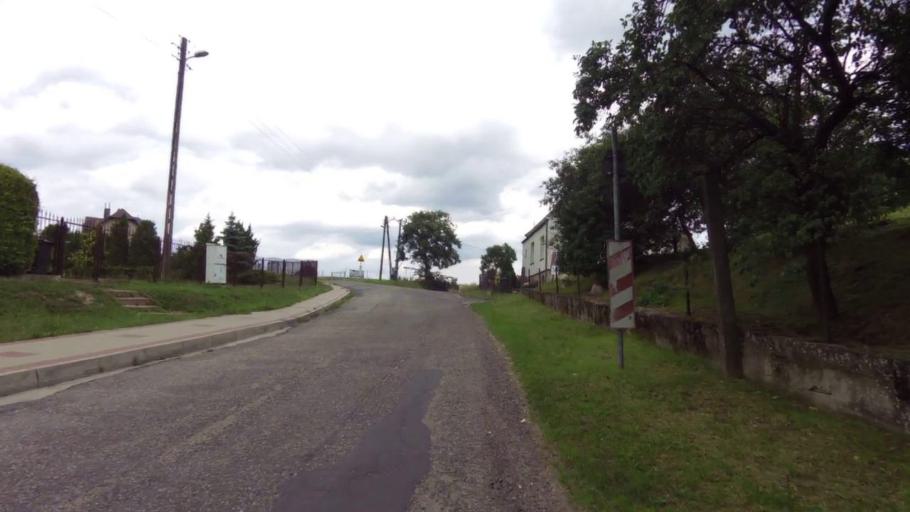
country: PL
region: West Pomeranian Voivodeship
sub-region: Powiat gryfinski
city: Moryn
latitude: 52.8724
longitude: 14.3904
